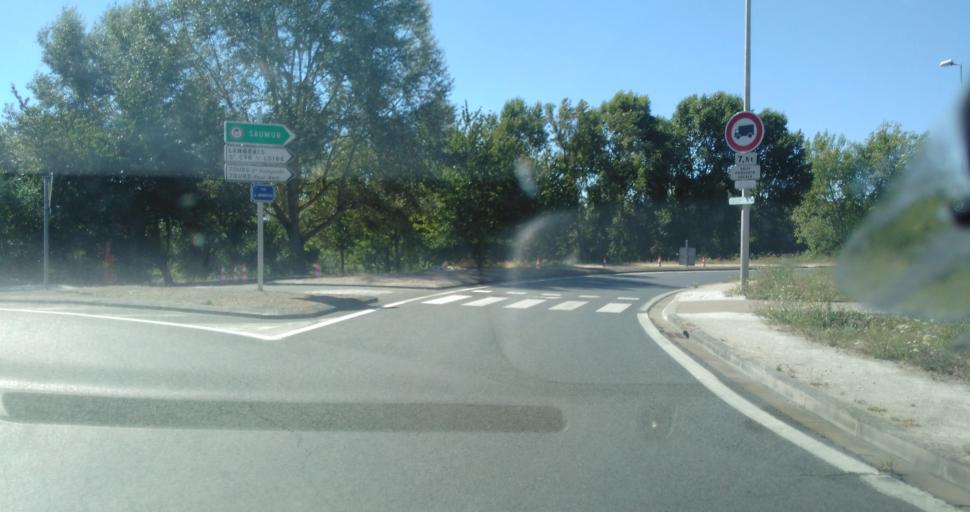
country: FR
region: Centre
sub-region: Departement d'Indre-et-Loire
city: Saint-Pierre-des-Corps
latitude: 47.4038
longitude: 0.7237
